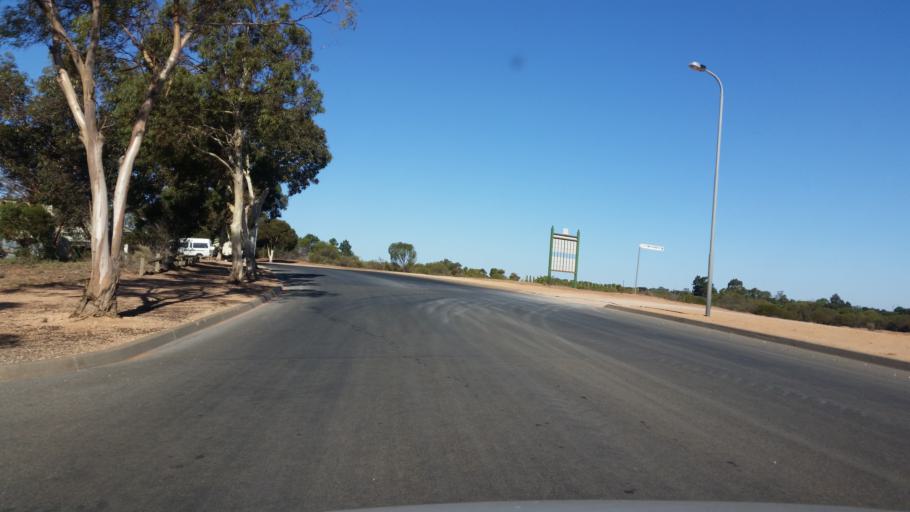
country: AU
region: South Australia
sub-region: Loxton Waikerie
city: Waikerie
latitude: -34.1889
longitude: 139.9817
